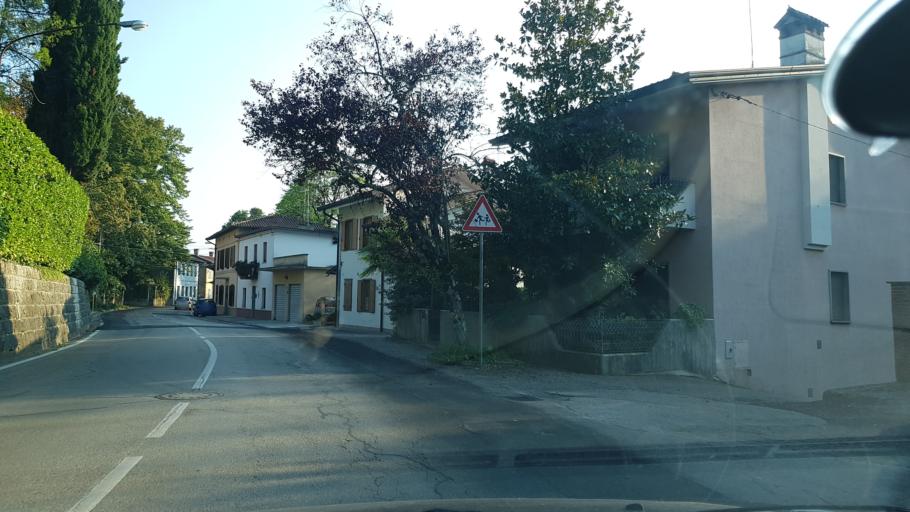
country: IT
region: Friuli Venezia Giulia
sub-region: Provincia di Gorizia
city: Gorizia
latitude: 45.9631
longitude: 13.6149
